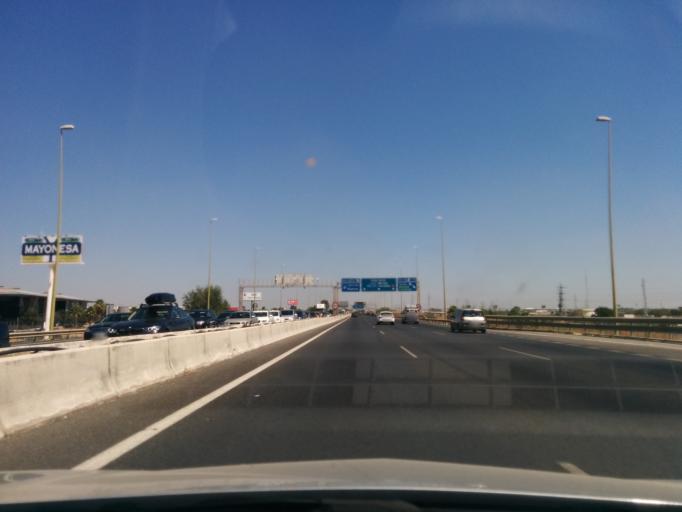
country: ES
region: Andalusia
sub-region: Provincia de Sevilla
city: Tomares
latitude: 37.3780
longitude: -6.0264
